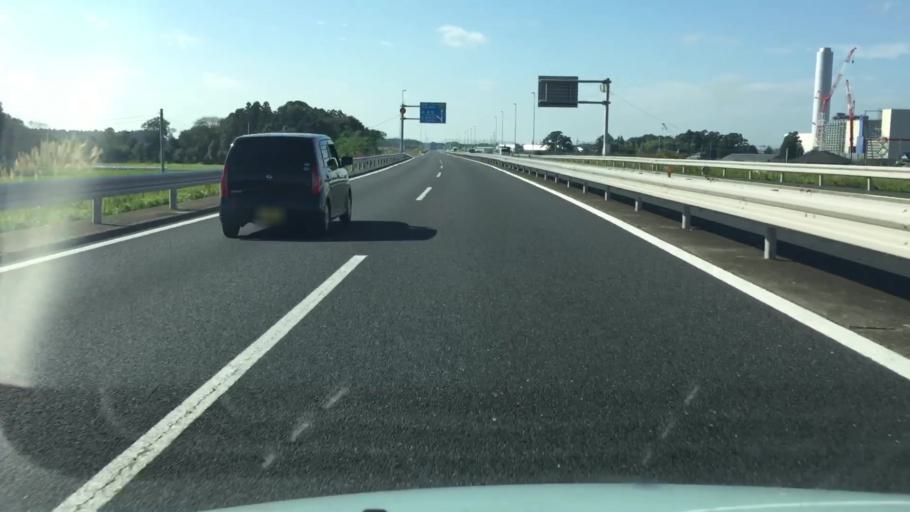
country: JP
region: Tochigi
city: Mooka
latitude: 36.4616
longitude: 139.9808
